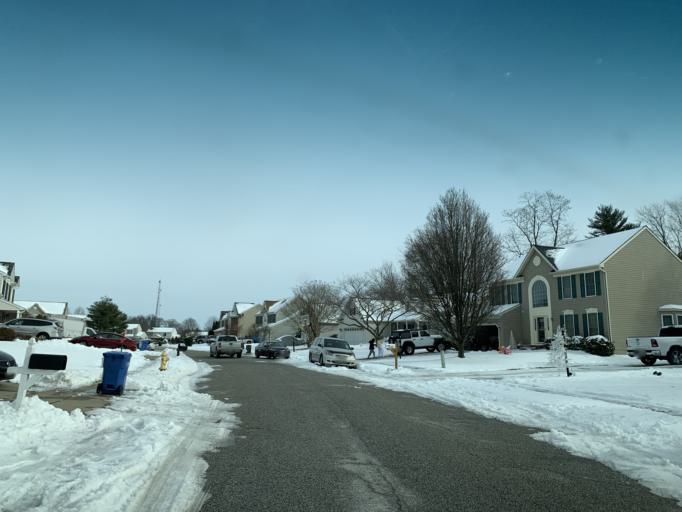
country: US
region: Maryland
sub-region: Harford County
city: Bel Air North
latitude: 39.5762
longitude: -76.3544
